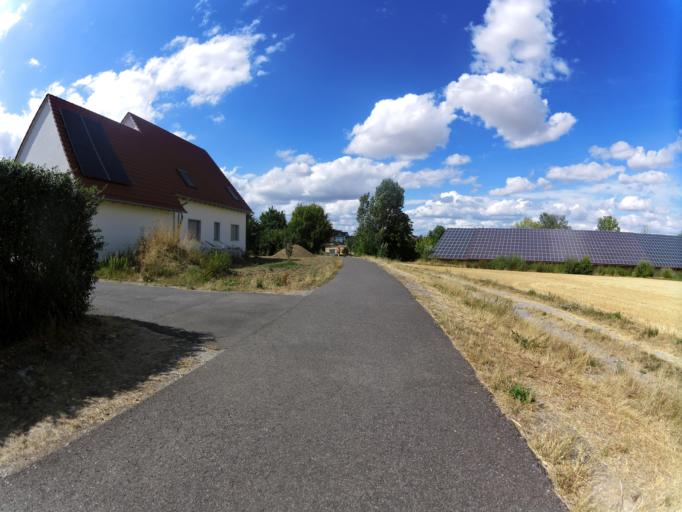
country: DE
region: Bavaria
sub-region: Regierungsbezirk Unterfranken
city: Sonderhofen
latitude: 49.5955
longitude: 10.0057
